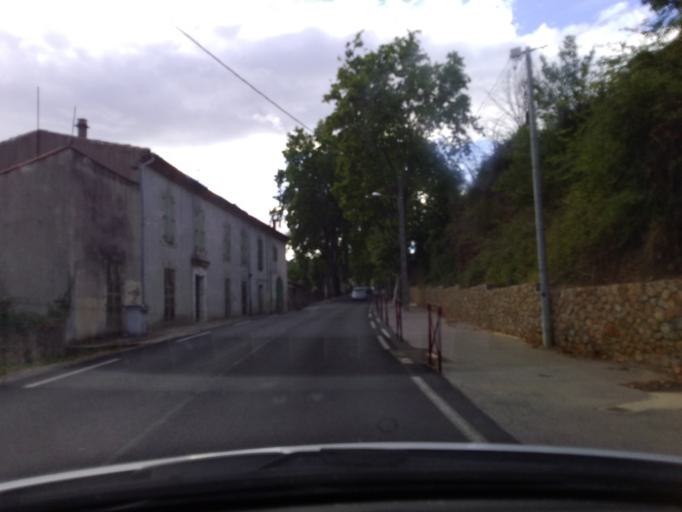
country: FR
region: Languedoc-Roussillon
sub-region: Departement de l'Herault
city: Nebian
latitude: 43.6264
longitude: 3.4246
